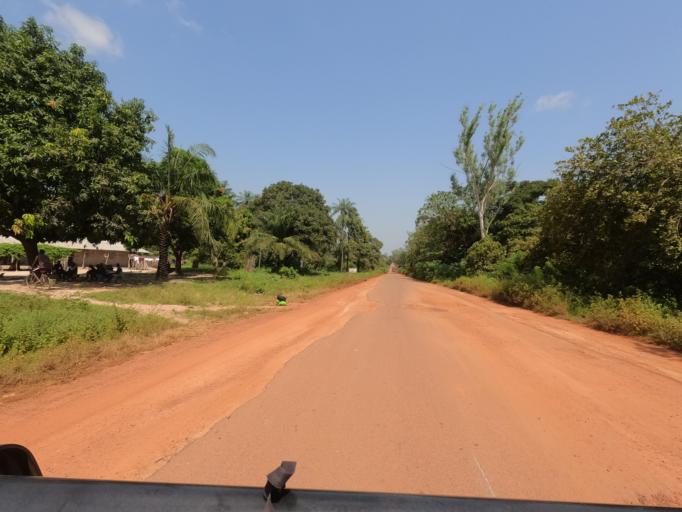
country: GW
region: Oio
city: Bissora
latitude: 12.3293
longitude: -15.7598
